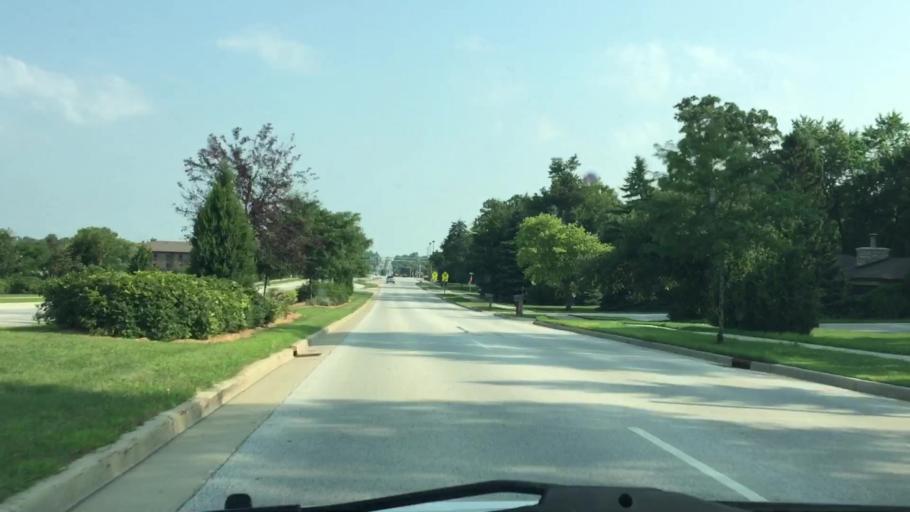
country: US
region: Wisconsin
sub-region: Waukesha County
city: Brookfield
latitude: 43.0325
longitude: -88.1269
